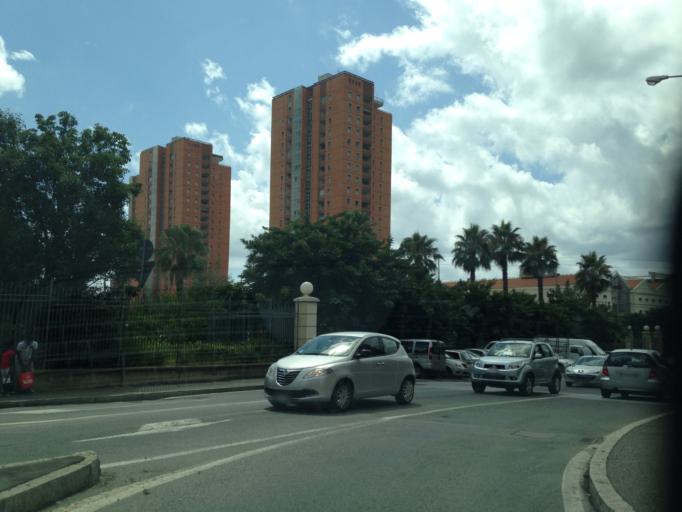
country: IT
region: Liguria
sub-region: Provincia di Genova
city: San Teodoro
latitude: 44.4147
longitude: 8.8820
